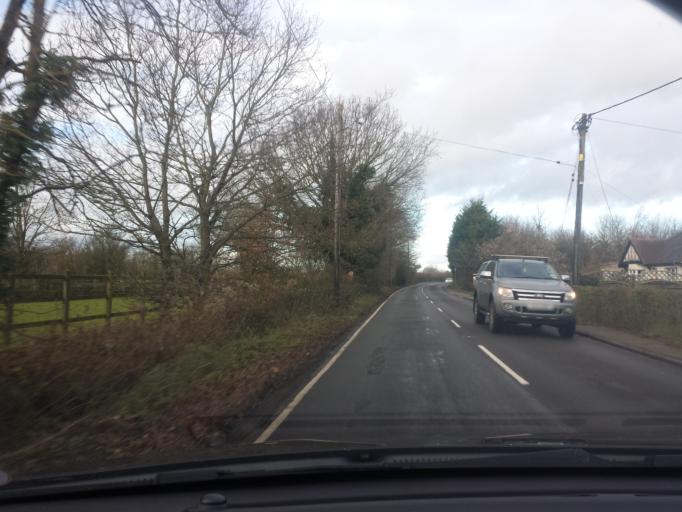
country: GB
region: England
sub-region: Essex
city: Alresford
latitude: 51.8820
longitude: 1.0325
